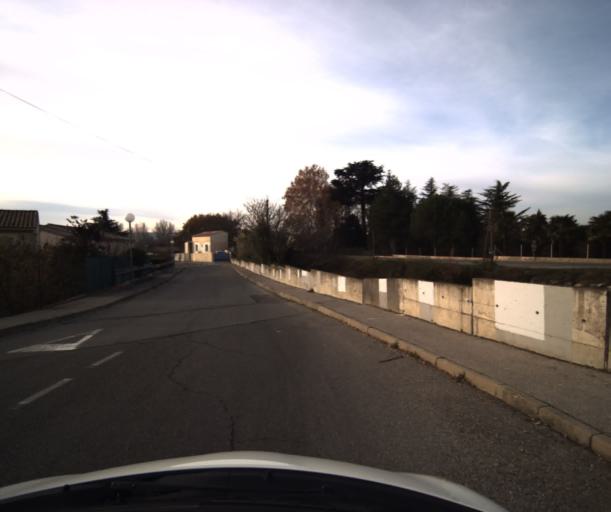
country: FR
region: Provence-Alpes-Cote d'Azur
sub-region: Departement du Vaucluse
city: Pertuis
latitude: 43.6917
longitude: 5.4921
